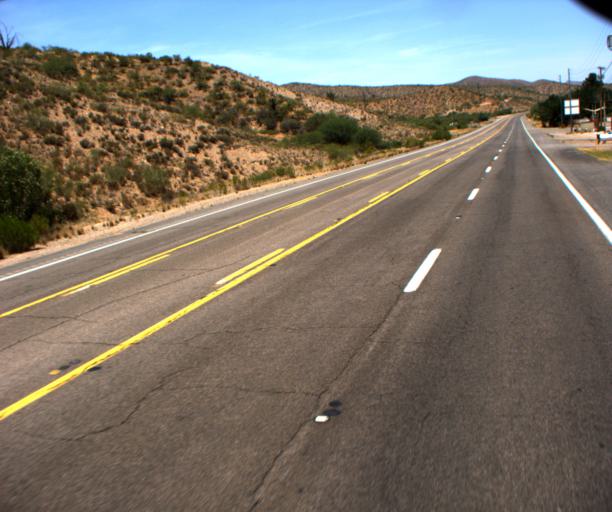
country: US
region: Arizona
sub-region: Gila County
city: Claypool
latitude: 33.4632
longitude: -110.8502
